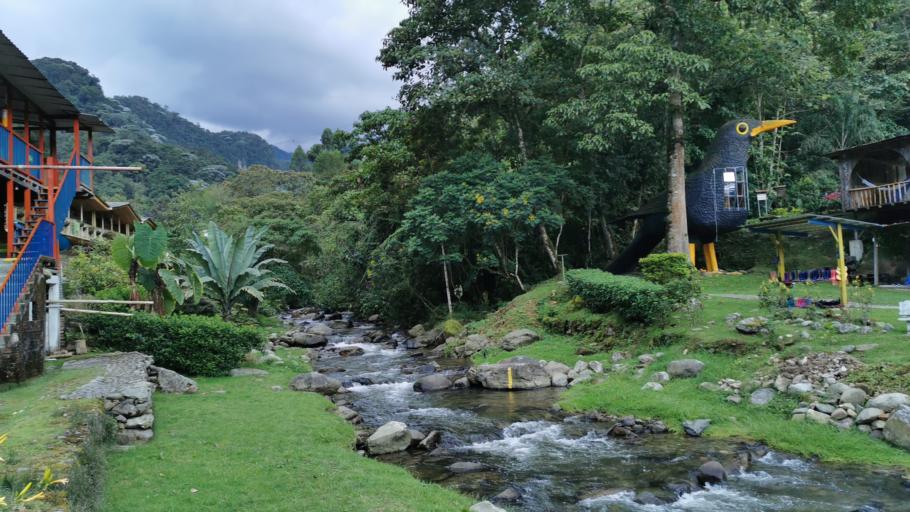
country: CO
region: Risaralda
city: Santa Rosa de Cabal
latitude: 4.8439
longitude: -75.5584
